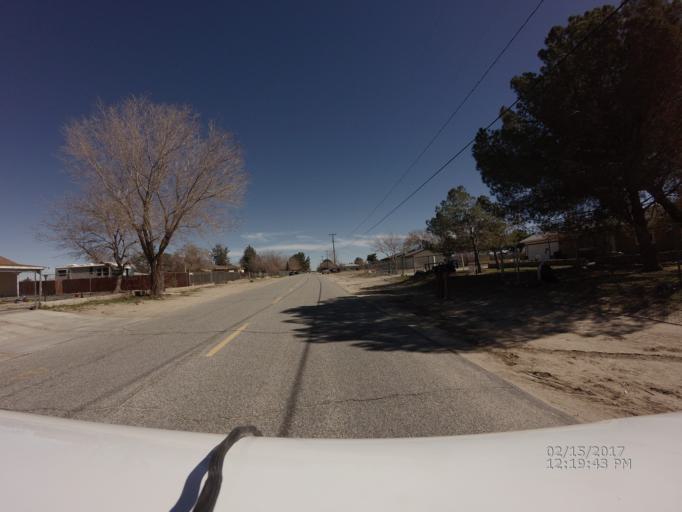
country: US
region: California
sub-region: Los Angeles County
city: Littlerock
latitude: 34.5780
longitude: -117.9492
